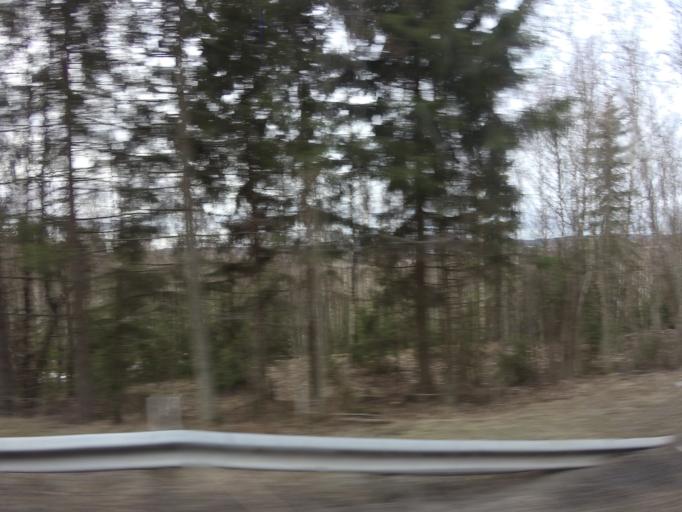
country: NO
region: Akershus
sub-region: Fet
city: Fetsund
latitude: 59.8909
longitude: 11.2004
